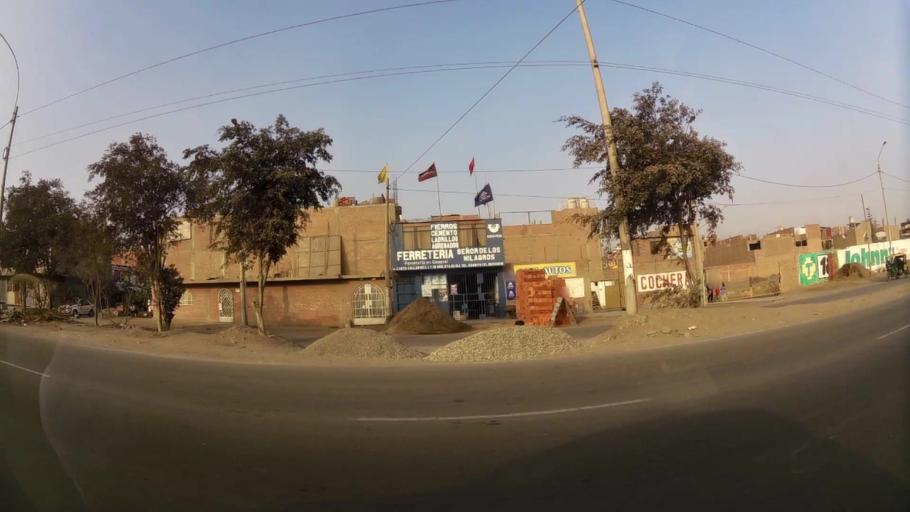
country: PE
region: Lima
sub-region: Lima
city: Independencia
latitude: -11.9656
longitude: -77.0832
